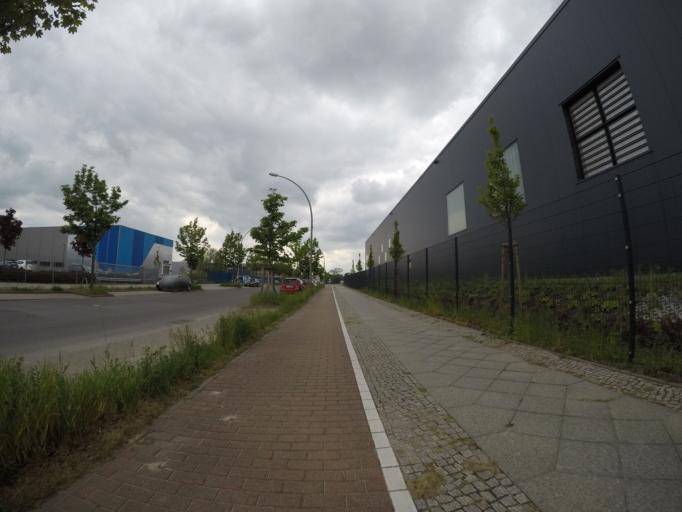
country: DE
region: Berlin
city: Falkenberg
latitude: 52.5488
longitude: 13.5369
